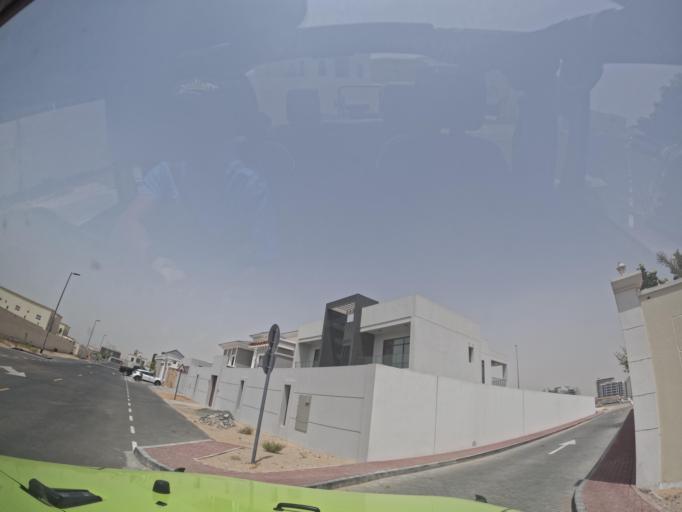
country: AE
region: Dubai
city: Dubai
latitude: 25.1272
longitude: 55.3722
